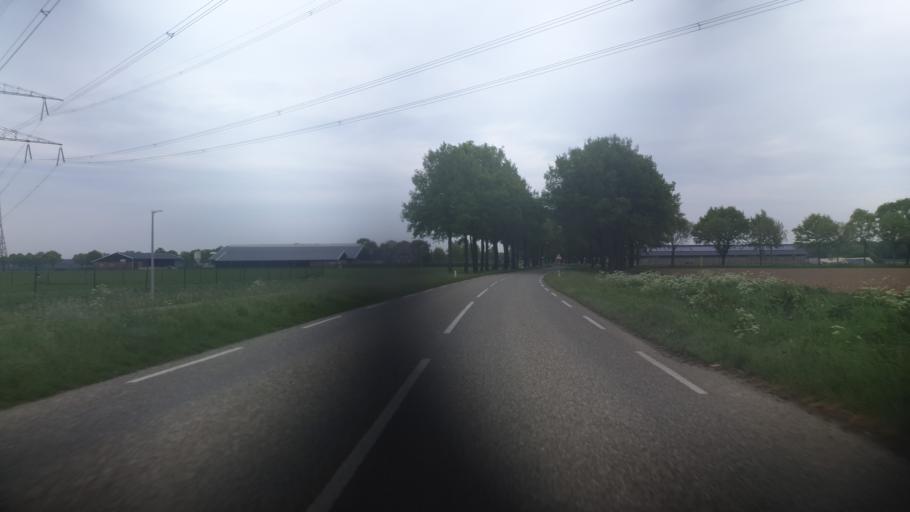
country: NL
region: North Brabant
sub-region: Gemeente Grave
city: Grave
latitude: 51.7699
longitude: 5.7896
